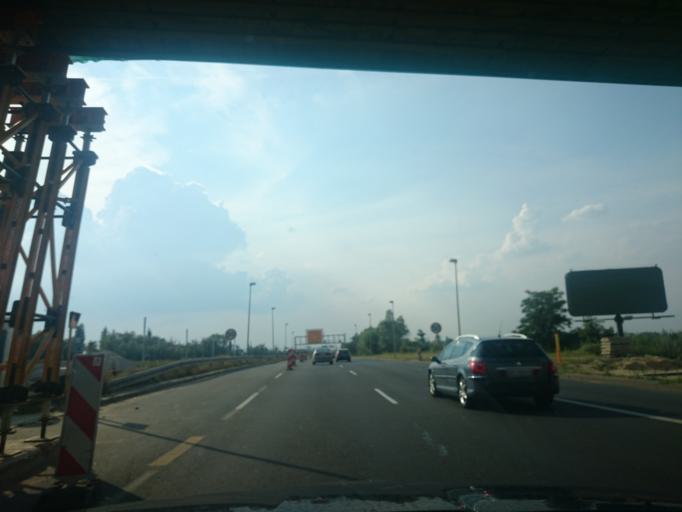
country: PL
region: West Pomeranian Voivodeship
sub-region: Szczecin
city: Szczecin
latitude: 53.3879
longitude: 14.6261
